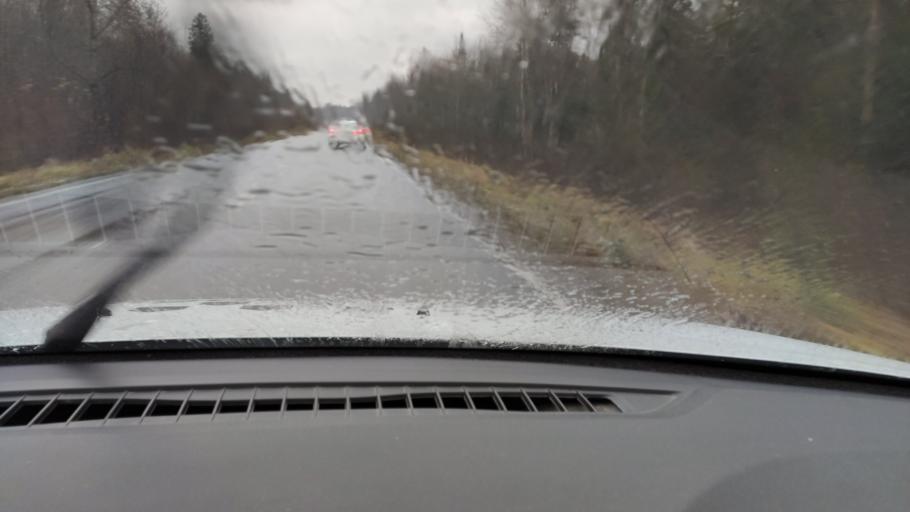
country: RU
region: Perm
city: Novyye Lyady
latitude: 58.0246
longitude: 56.6365
